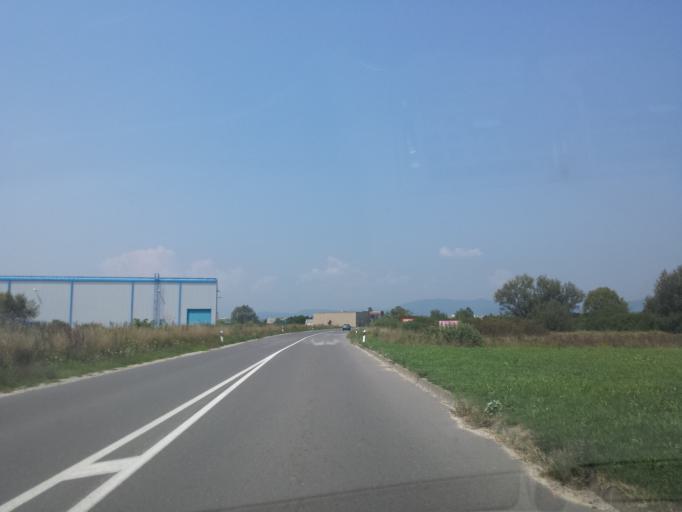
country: HR
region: Zagrebacka
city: Jastrebarsko
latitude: 45.6521
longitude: 15.6598
